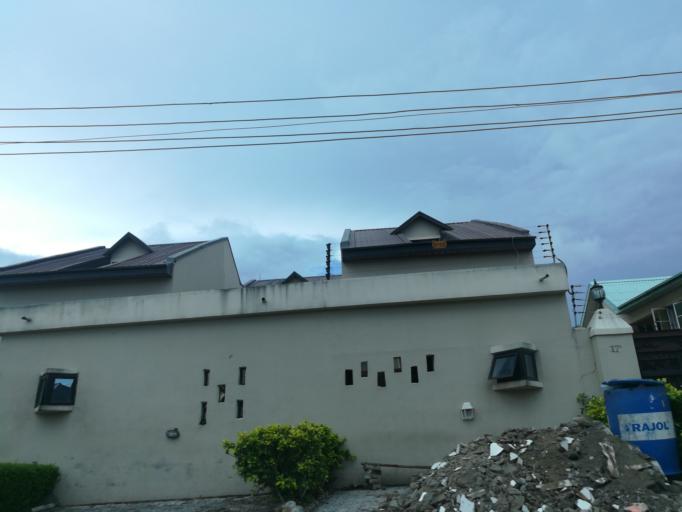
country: NG
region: Lagos
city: Ikoyi
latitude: 6.4443
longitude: 3.4739
